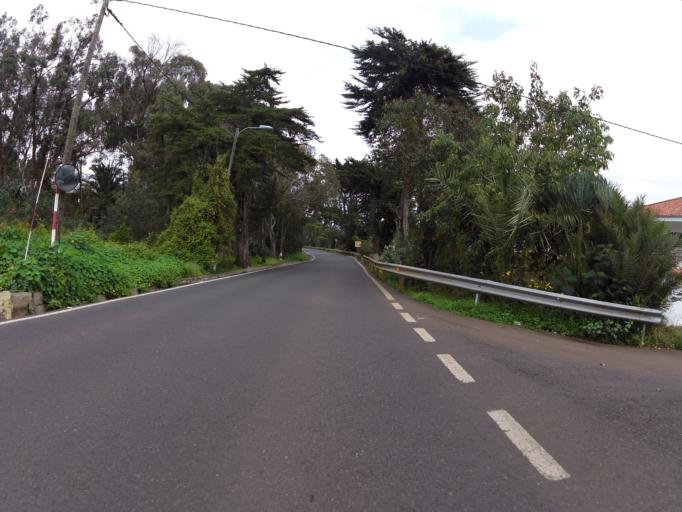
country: ES
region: Canary Islands
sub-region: Provincia de Las Palmas
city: Firgas
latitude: 28.0923
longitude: -15.5370
